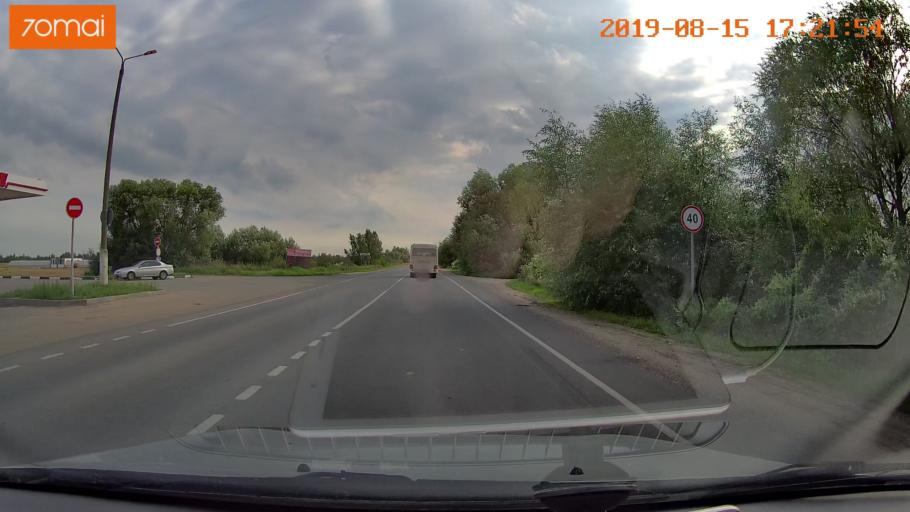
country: RU
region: Moskovskaya
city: Ashitkovo
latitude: 55.4190
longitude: 38.5663
